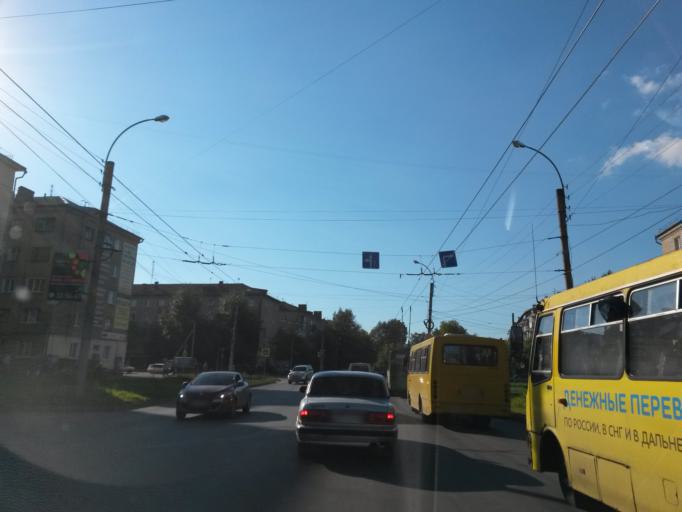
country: RU
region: Ivanovo
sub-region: Gorod Ivanovo
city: Ivanovo
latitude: 56.9840
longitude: 40.9618
